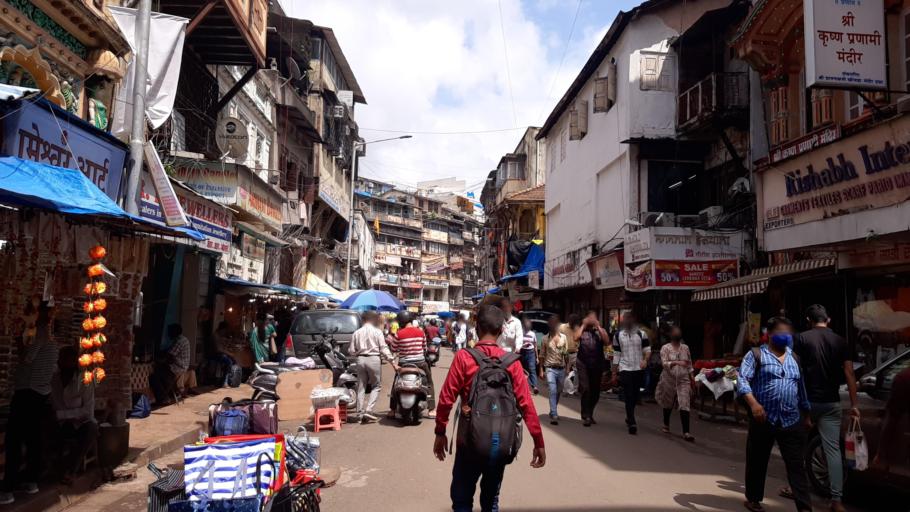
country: IN
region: Maharashtra
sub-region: Mumbai Suburban
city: Mumbai
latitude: 18.9532
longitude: 72.8283
